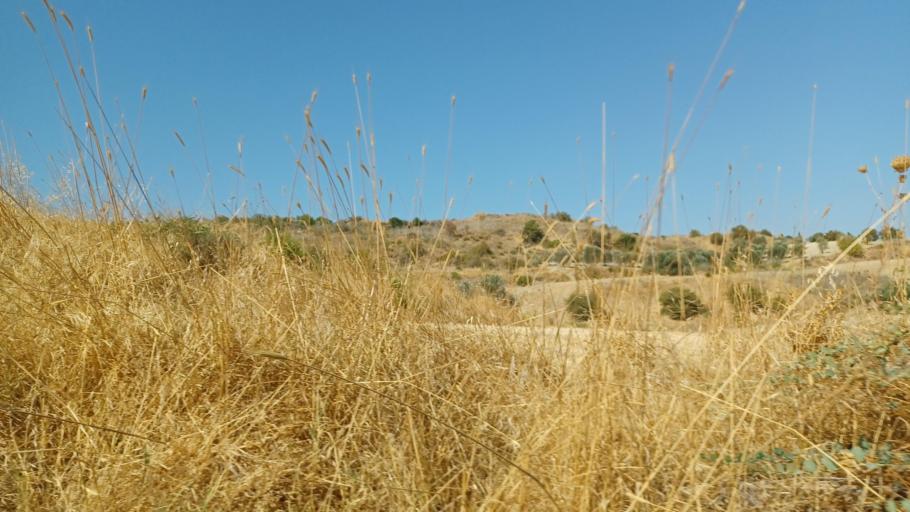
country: CY
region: Pafos
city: Polis
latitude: 34.9460
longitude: 32.5132
